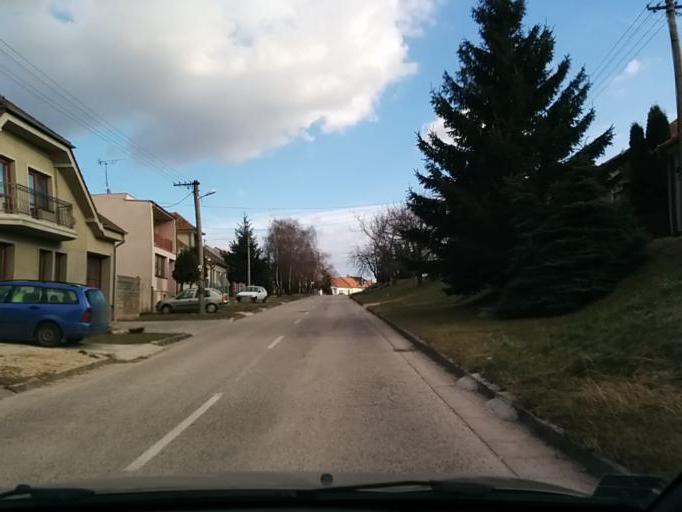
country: SK
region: Trnavsky
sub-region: Okres Trnava
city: Trnava
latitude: 48.3322
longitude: 17.5967
